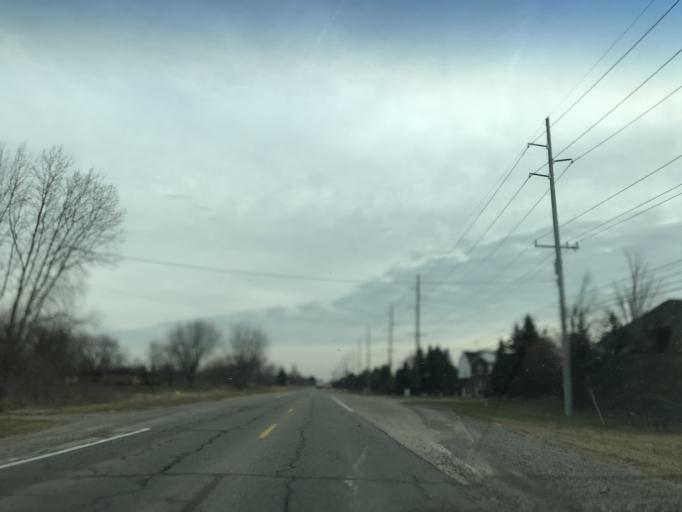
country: US
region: Michigan
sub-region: Macomb County
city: Mount Clemens
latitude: 42.6727
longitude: -82.9148
